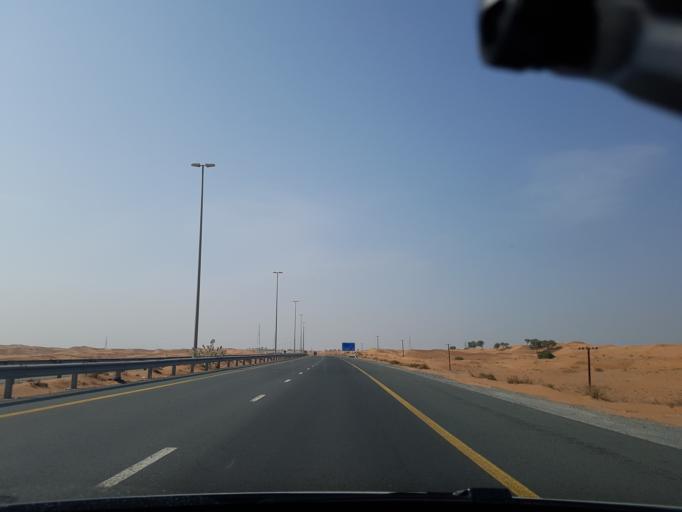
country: AE
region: Umm al Qaywayn
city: Umm al Qaywayn
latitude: 25.5202
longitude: 55.7398
